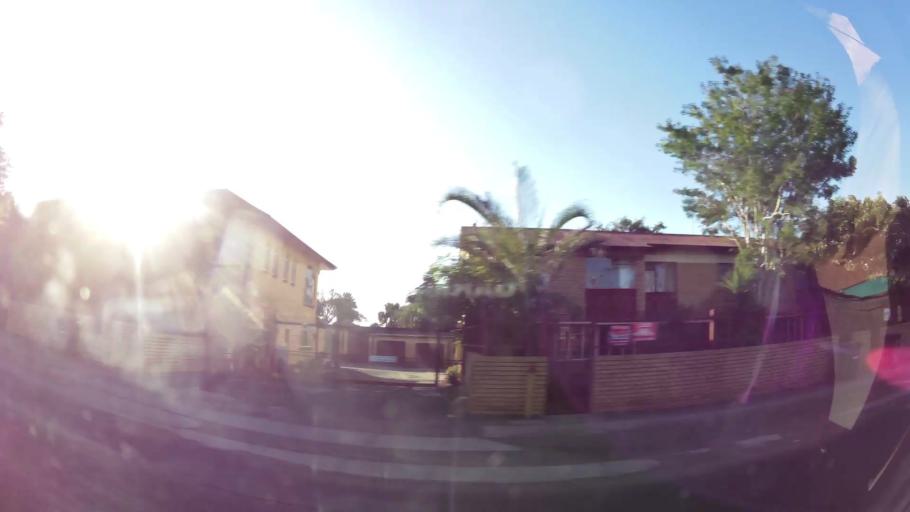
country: ZA
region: Gauteng
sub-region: City of Tshwane Metropolitan Municipality
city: Pretoria
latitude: -25.7244
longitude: 28.2075
